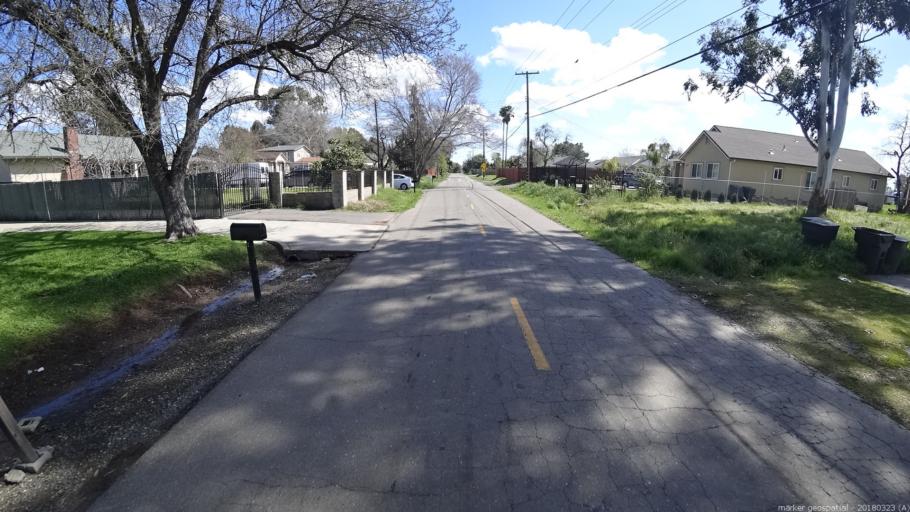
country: US
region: California
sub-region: Sacramento County
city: North Highlands
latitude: 38.6834
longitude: -121.4091
